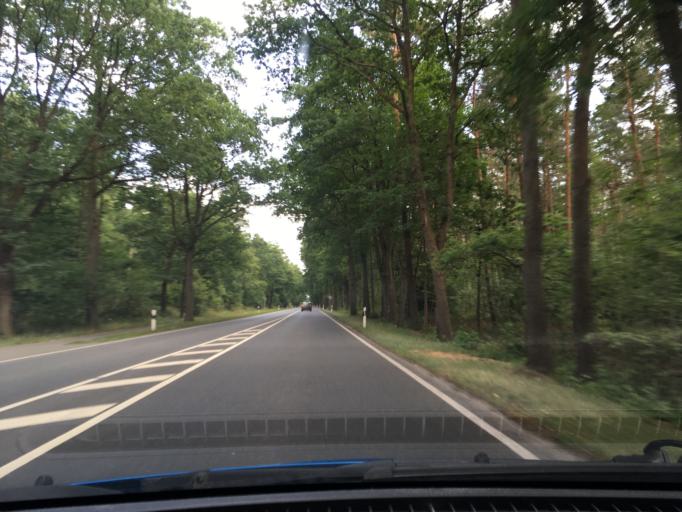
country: DE
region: Lower Saxony
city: Kakenstorf
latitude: 53.2856
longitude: 9.7944
